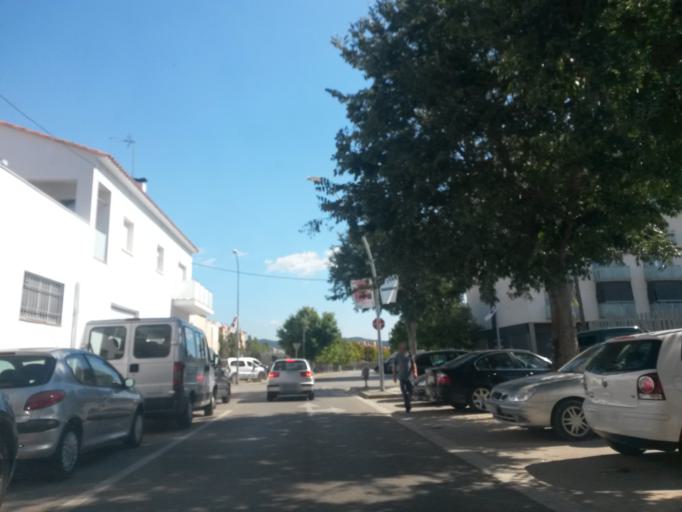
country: ES
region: Catalonia
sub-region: Provincia de Girona
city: Salt
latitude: 41.9724
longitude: 2.7972
